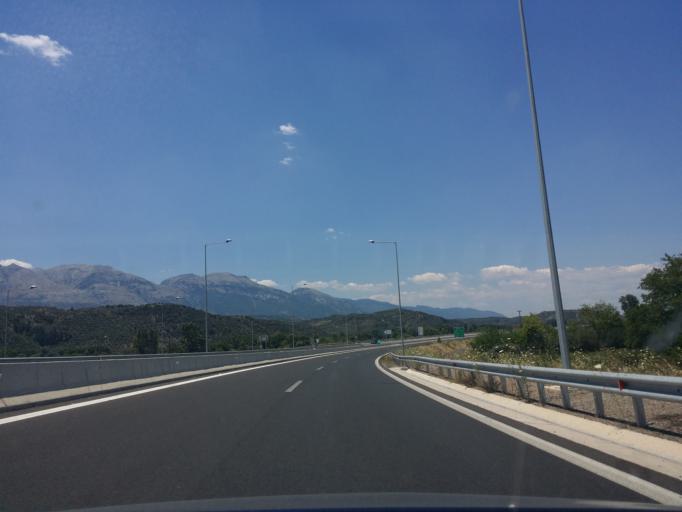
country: GR
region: Peloponnese
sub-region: Nomos Lakonias
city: Sparti
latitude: 37.0945
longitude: 22.4309
